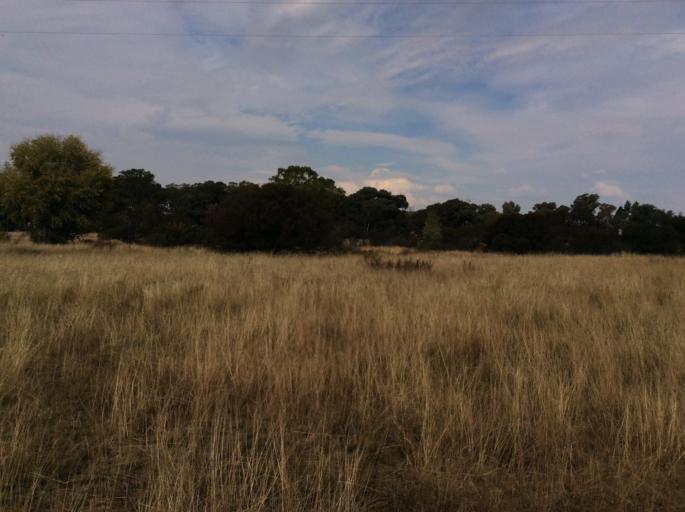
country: ZA
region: Orange Free State
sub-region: Xhariep District Municipality
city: Dewetsdorp
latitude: -29.5755
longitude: 26.6746
